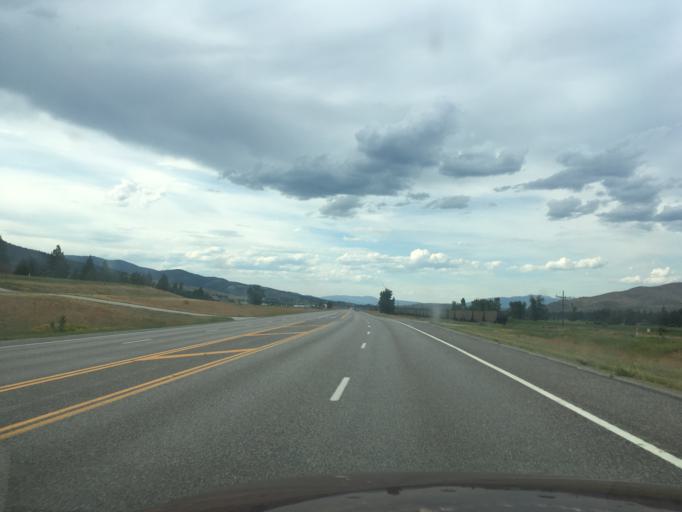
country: US
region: Montana
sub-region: Missoula County
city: Lolo
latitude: 46.6974
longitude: -114.0740
